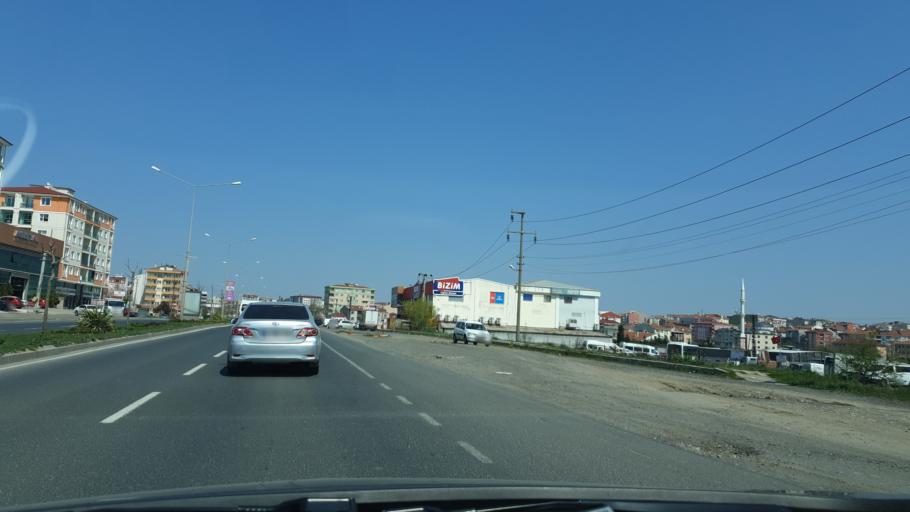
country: TR
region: Tekirdag
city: Corlu
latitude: 41.1558
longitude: 27.7824
